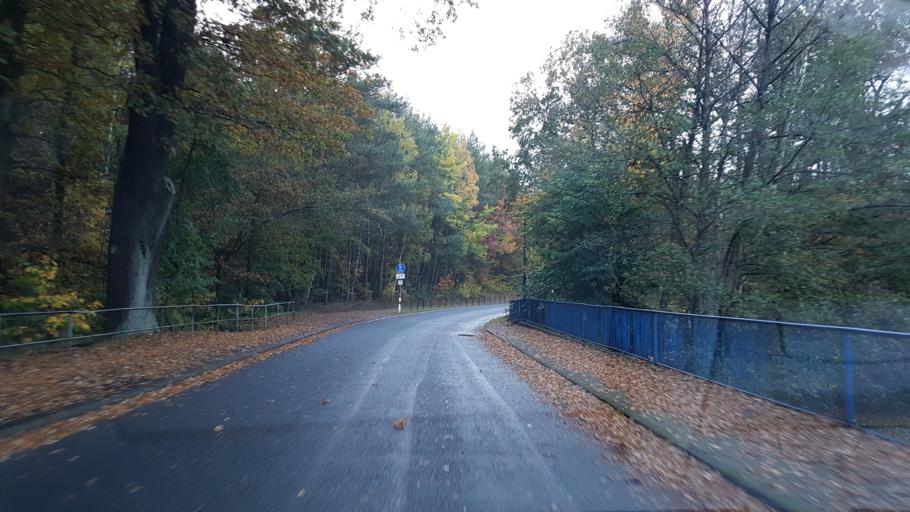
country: DE
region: Saxony
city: Dahlen
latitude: 51.3952
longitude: 13.0030
